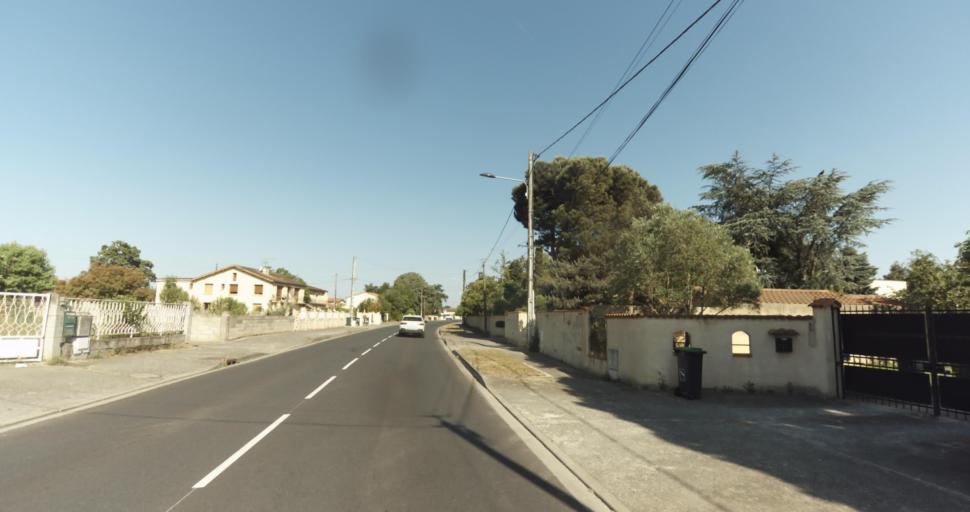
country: FR
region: Midi-Pyrenees
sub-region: Departement de la Haute-Garonne
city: Plaisance-du-Touch
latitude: 43.5538
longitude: 1.3081
